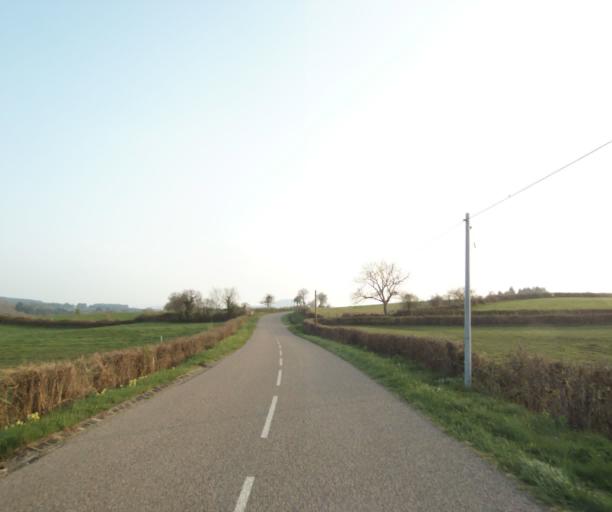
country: FR
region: Bourgogne
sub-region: Departement de Saone-et-Loire
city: Charolles
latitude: 46.4505
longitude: 4.4296
